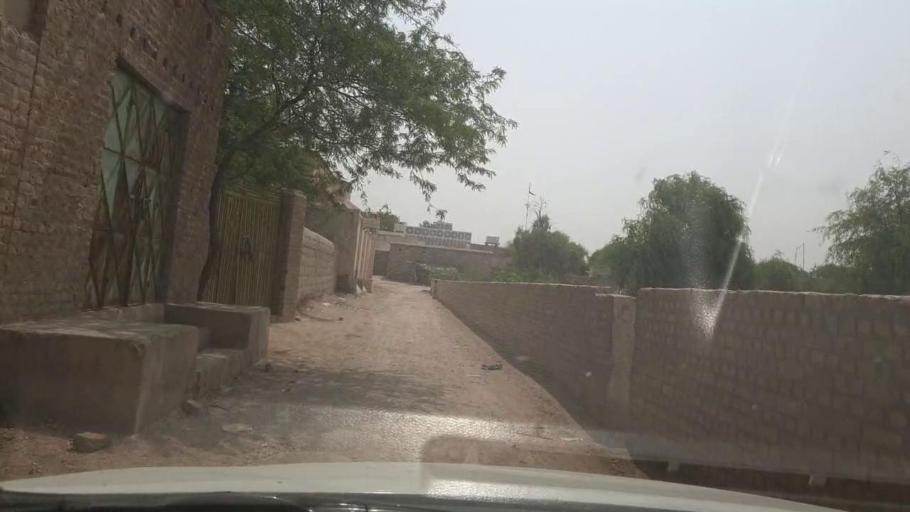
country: PK
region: Sindh
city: Kot Diji
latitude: 27.3384
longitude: 68.7088
